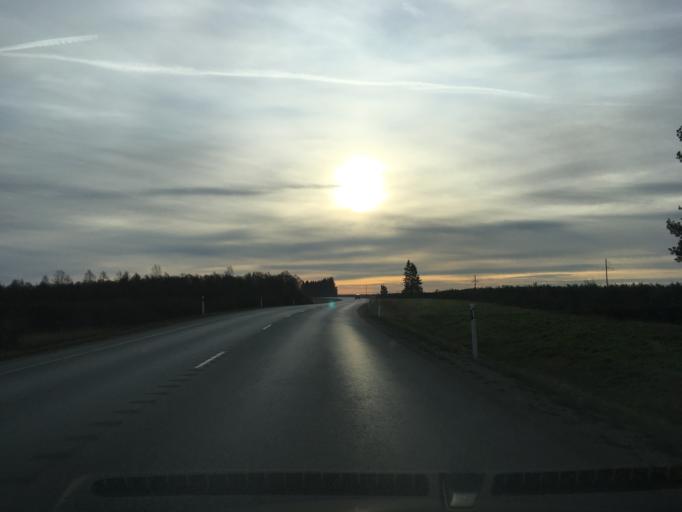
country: EE
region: Ida-Virumaa
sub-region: Kivioli linn
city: Kivioli
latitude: 59.4204
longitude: 26.9705
